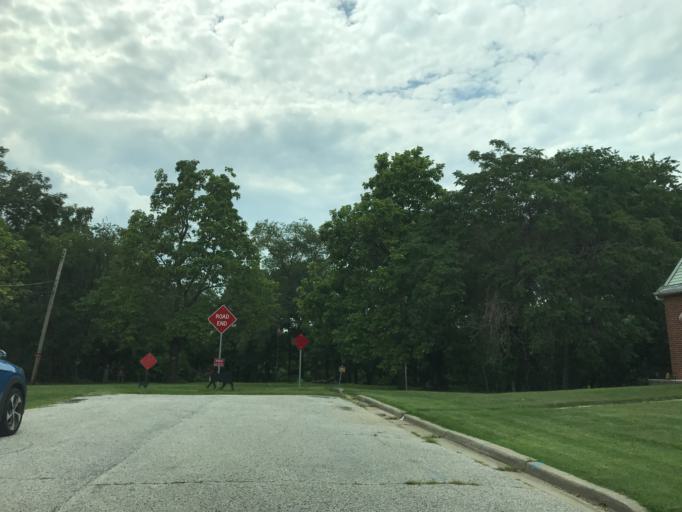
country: US
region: Maryland
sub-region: Baltimore County
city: Essex
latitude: 39.3163
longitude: -76.4849
